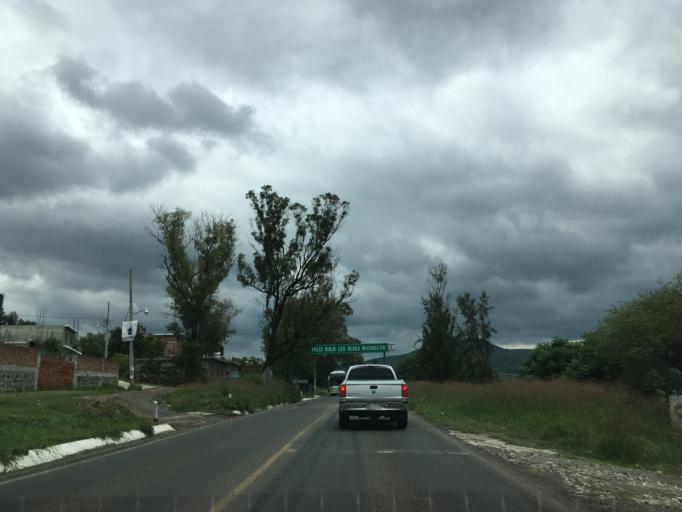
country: MX
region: Guanajuato
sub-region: Moroleon
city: Rinconadas del Bosque
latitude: 20.0817
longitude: -101.1563
